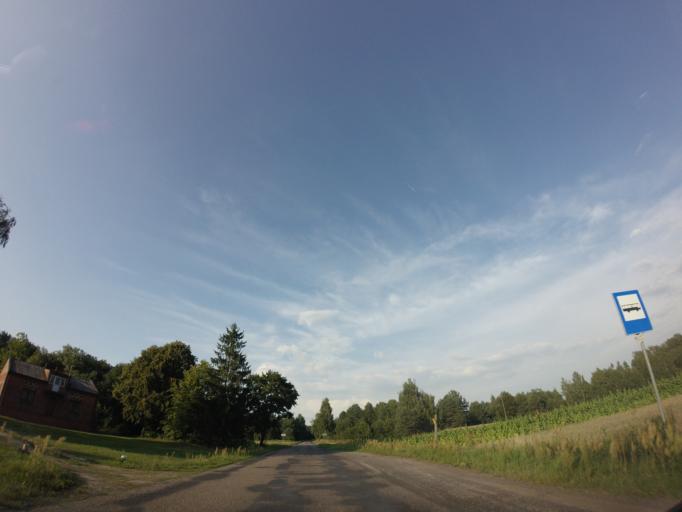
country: PL
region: Lublin Voivodeship
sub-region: Powiat pulawski
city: Kurow
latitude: 51.4266
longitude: 22.2079
